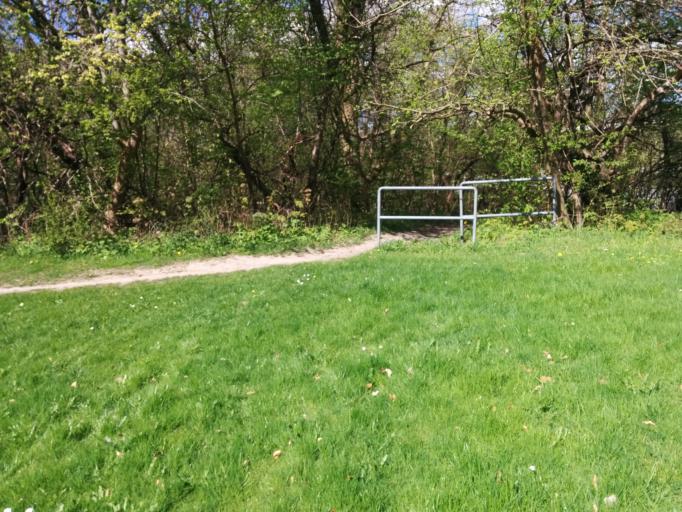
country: DK
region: Central Jutland
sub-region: Arhus Kommune
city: Stavtrup
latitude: 56.1270
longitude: 10.1334
